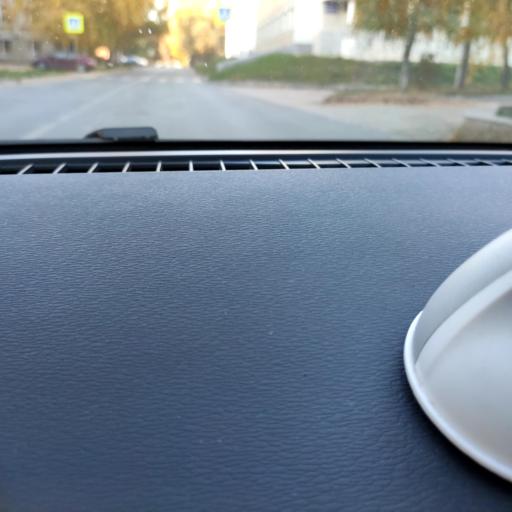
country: RU
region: Samara
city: Samara
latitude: 53.2291
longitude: 50.2339
